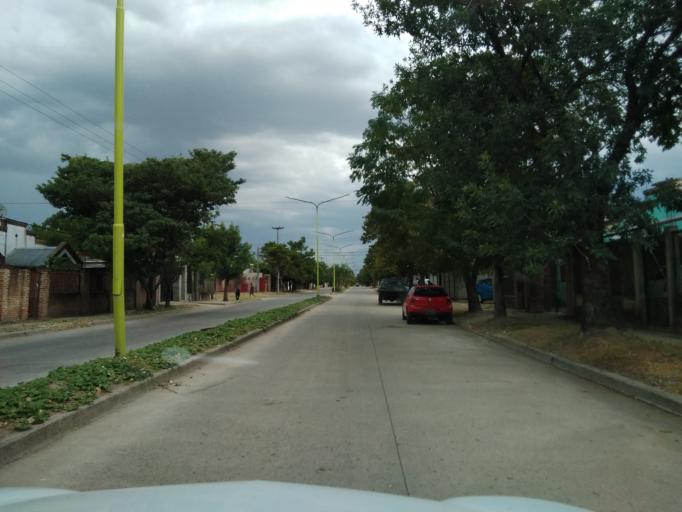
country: AR
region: Corrientes
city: Corrientes
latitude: -27.5185
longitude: -58.7916
